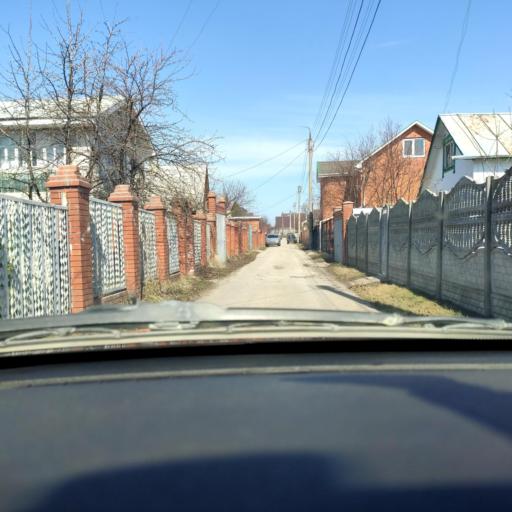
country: RU
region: Samara
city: Podstepki
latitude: 53.5057
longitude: 49.1665
